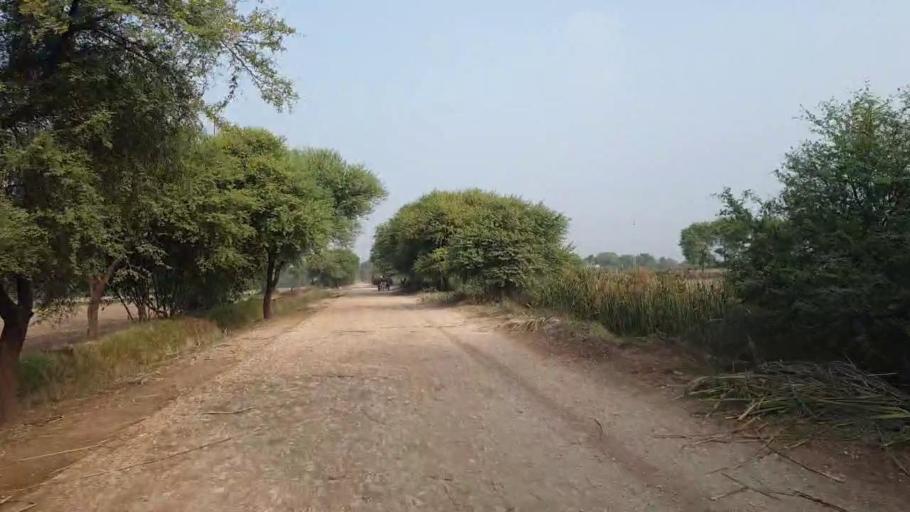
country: PK
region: Sindh
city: Tando Muhammad Khan
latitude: 25.1378
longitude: 68.5930
